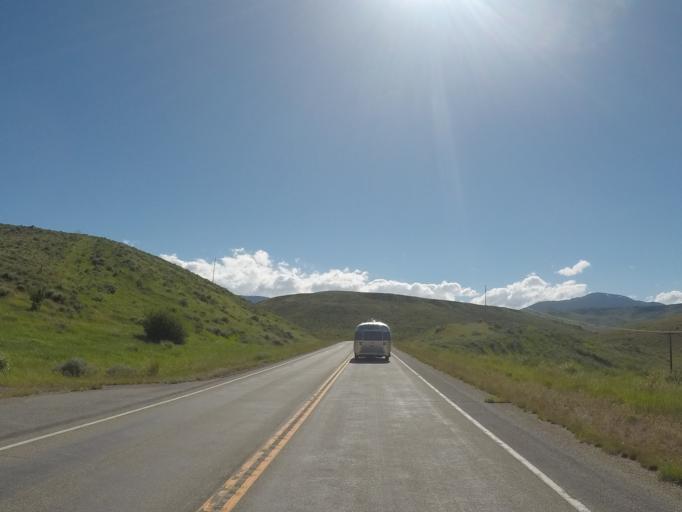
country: US
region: Montana
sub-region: Carbon County
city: Red Lodge
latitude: 45.1575
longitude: -109.1797
